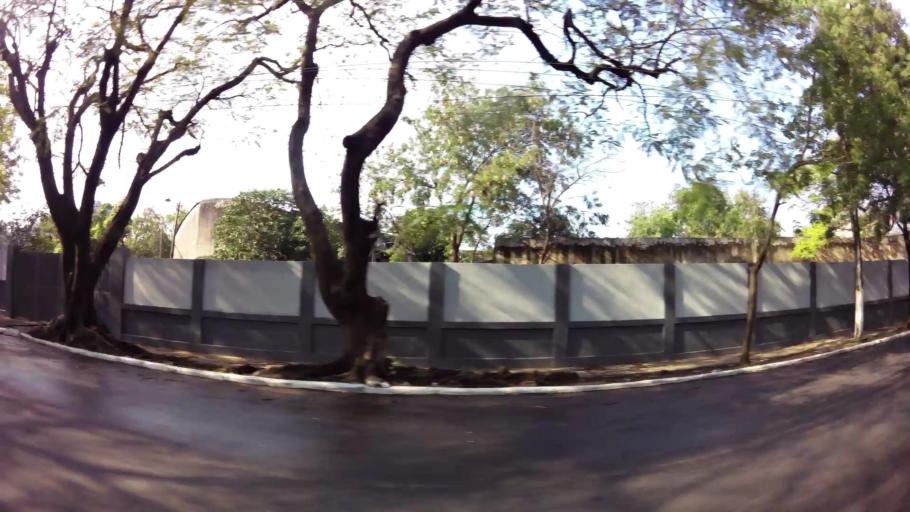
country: PY
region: Asuncion
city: Asuncion
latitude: -25.2765
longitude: -57.6433
